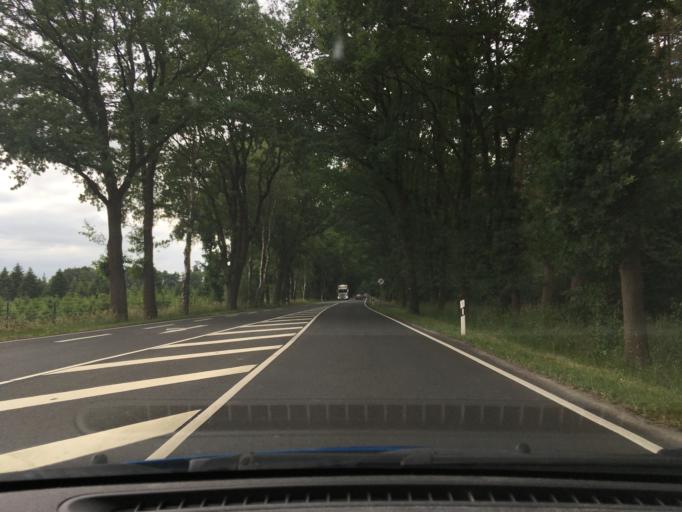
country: DE
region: Lower Saxony
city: Wenzendorf
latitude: 53.3464
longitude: 9.8100
